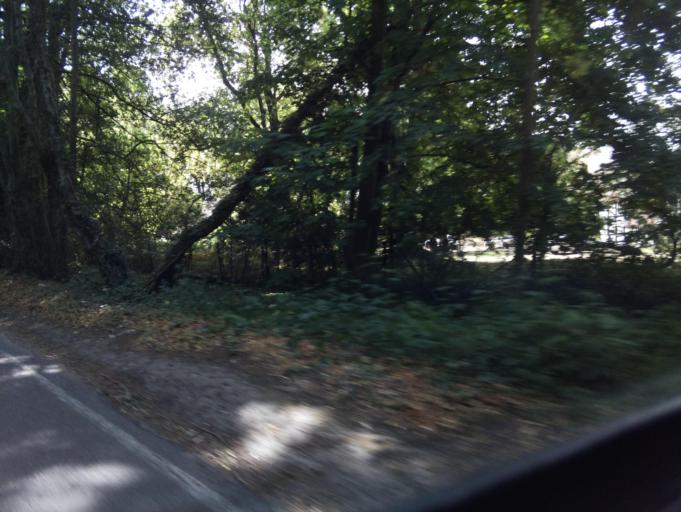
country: GB
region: England
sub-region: Surrey
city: Pirbright
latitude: 51.3064
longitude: -0.6521
